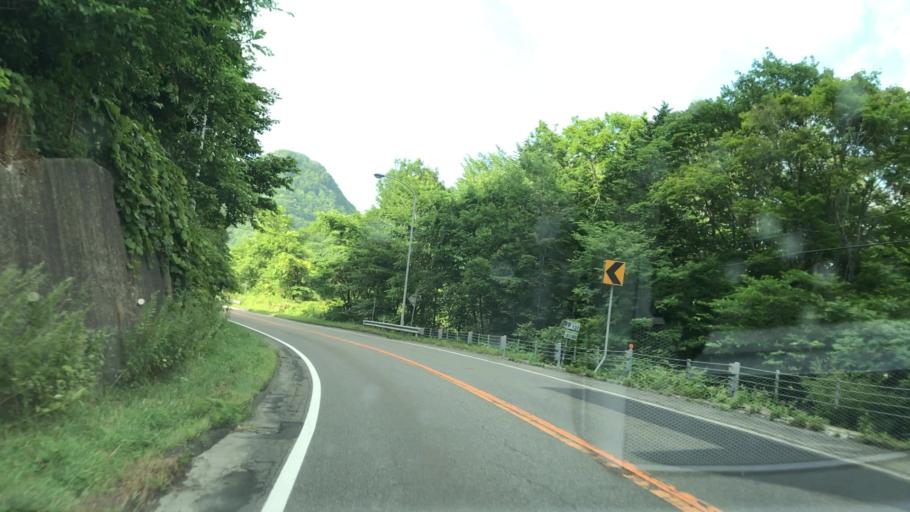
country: JP
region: Hokkaido
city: Shizunai-furukawacho
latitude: 42.8004
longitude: 142.3977
